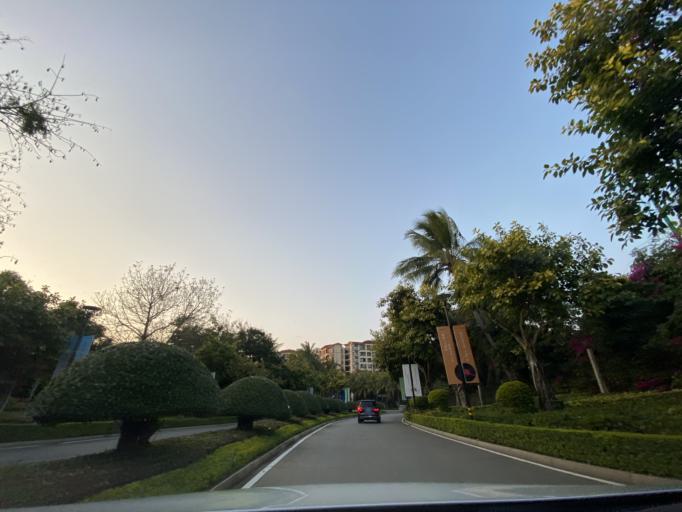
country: CN
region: Hainan
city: Yingzhou
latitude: 18.3960
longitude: 109.8559
